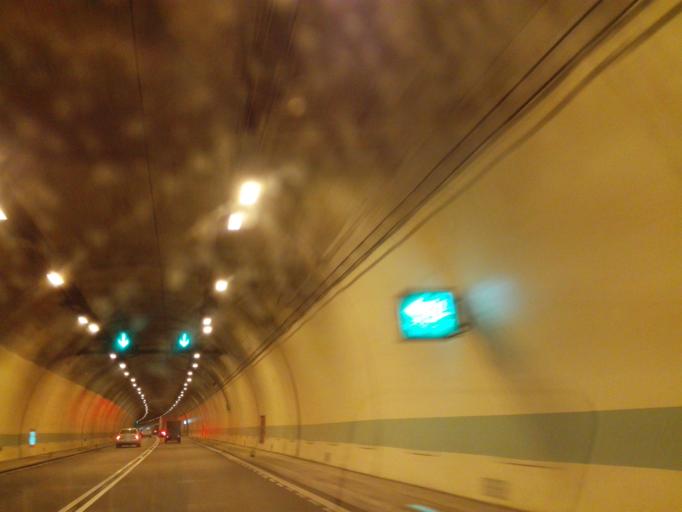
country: TW
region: Taiwan
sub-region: Nantou
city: Puli
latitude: 24.0008
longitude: 120.8412
